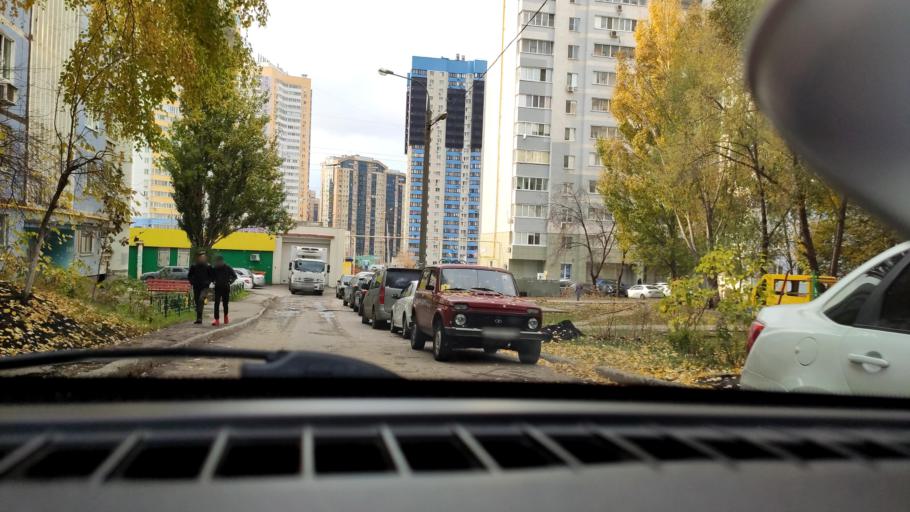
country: RU
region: Samara
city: Samara
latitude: 53.2408
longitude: 50.1905
